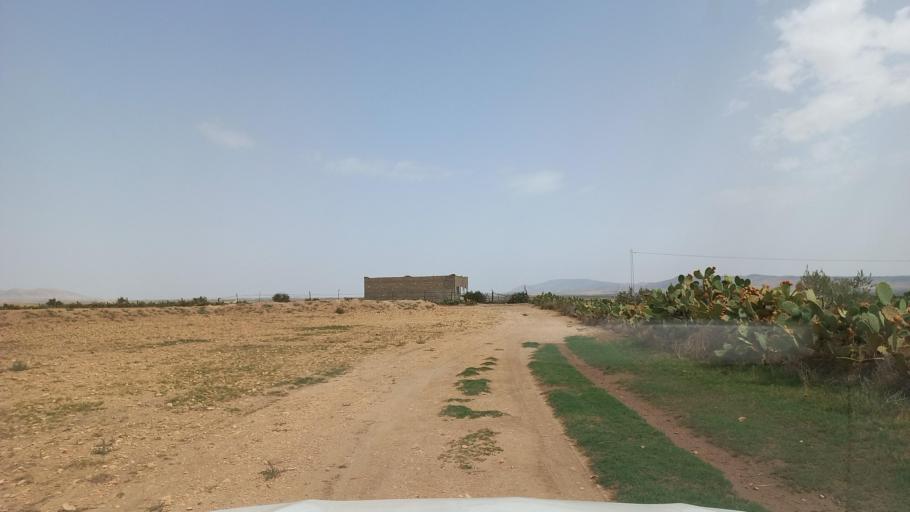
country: TN
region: Al Qasrayn
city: Kasserine
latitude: 35.2899
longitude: 9.0053
